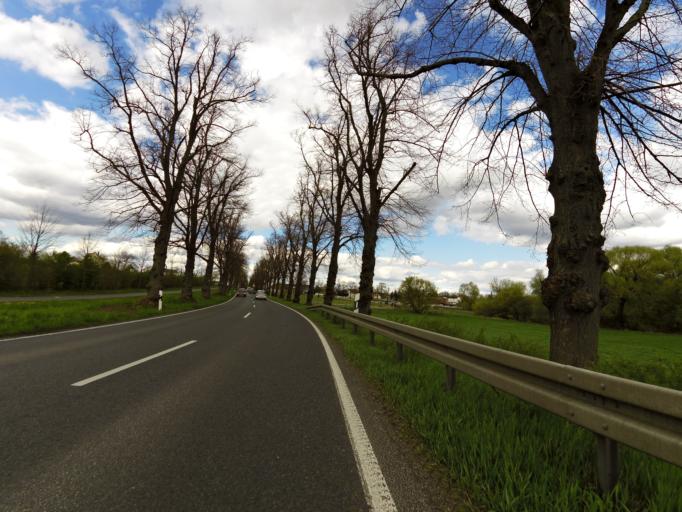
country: DE
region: Berlin
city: Lichtenrade
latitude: 52.3915
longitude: 13.4433
